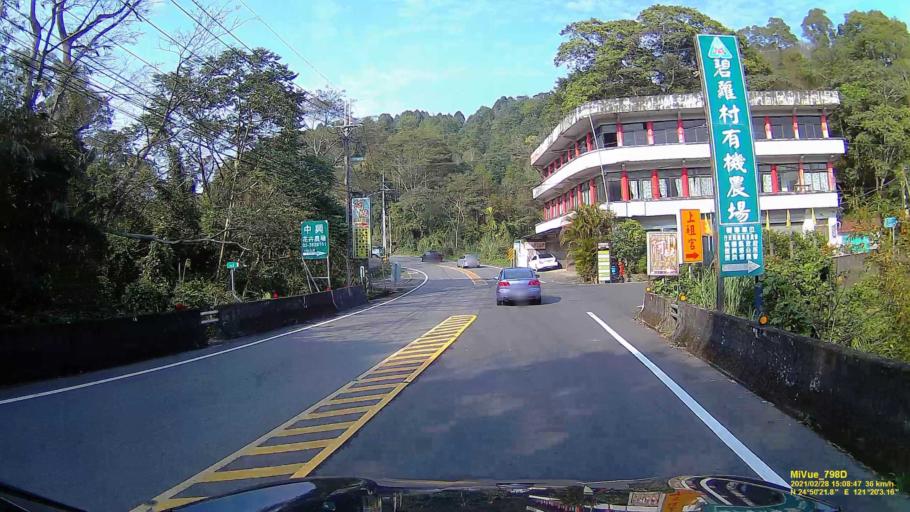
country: TW
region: Taiwan
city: Daxi
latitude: 24.8396
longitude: 121.3342
